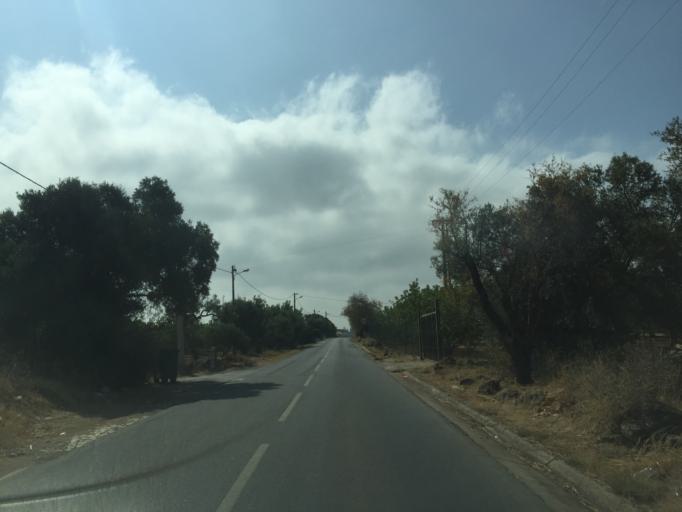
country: PT
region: Faro
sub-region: Olhao
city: Olhao
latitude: 37.0780
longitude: -7.8905
